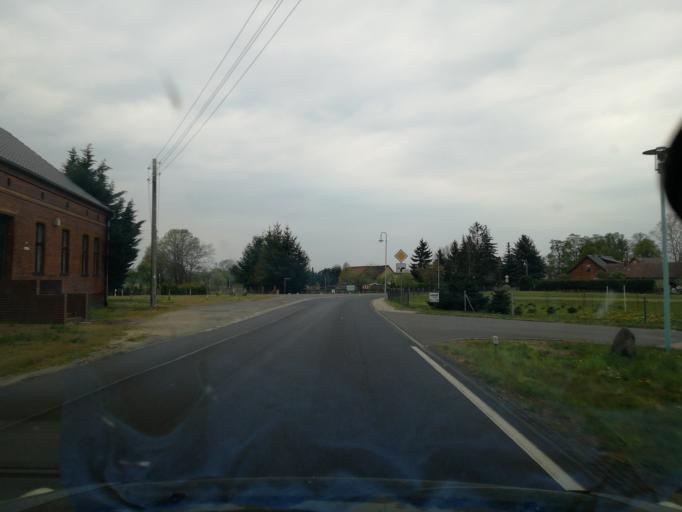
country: DE
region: Brandenburg
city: Calau
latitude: 51.7596
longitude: 13.9147
